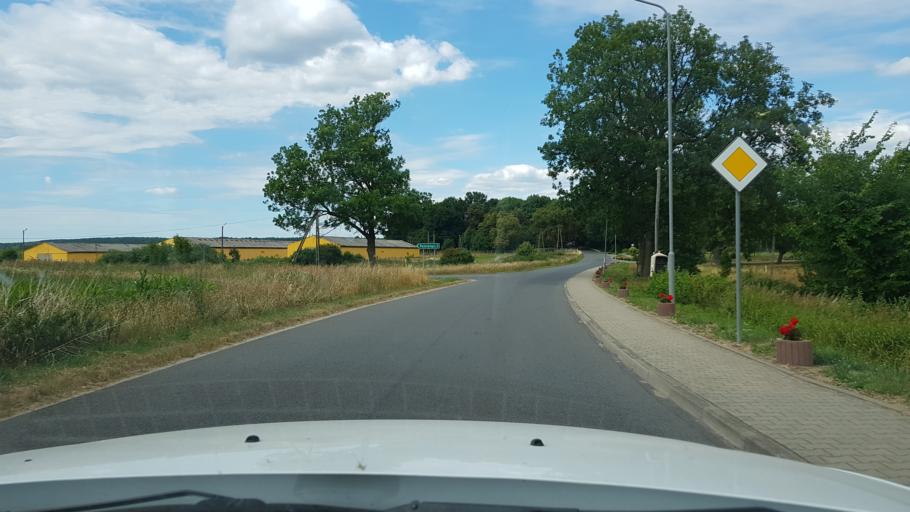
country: PL
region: West Pomeranian Voivodeship
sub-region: Powiat drawski
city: Kalisz Pomorski
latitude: 53.3351
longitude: 15.9319
